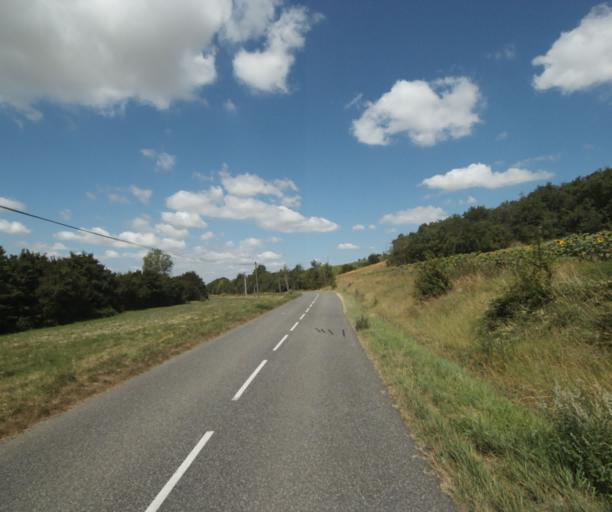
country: FR
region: Midi-Pyrenees
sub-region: Departement de la Haute-Garonne
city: Auriac-sur-Vendinelle
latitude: 43.4796
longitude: 1.8008
